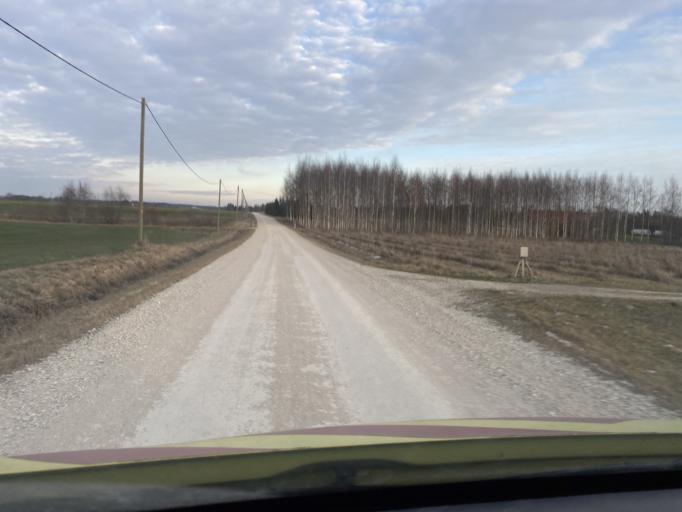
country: EE
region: Jogevamaa
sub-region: Poltsamaa linn
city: Poltsamaa
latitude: 58.5848
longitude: 26.1813
